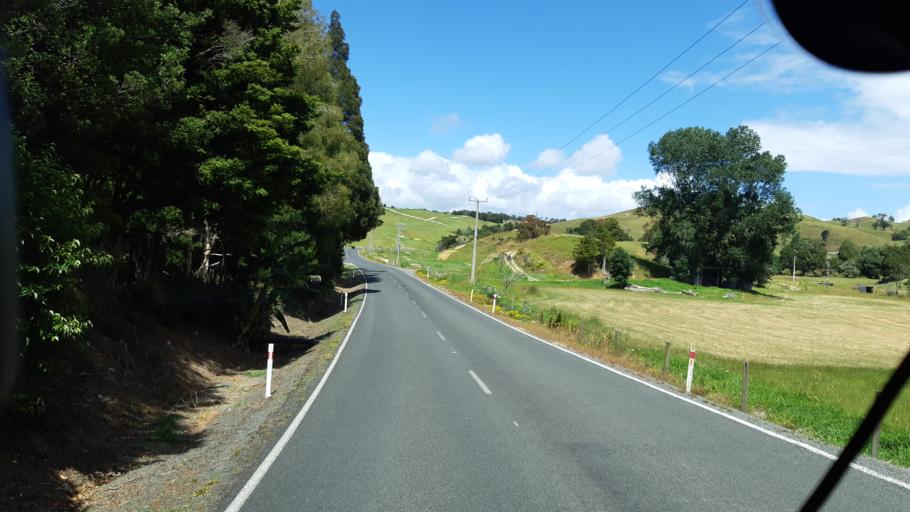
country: NZ
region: Northland
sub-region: Far North District
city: Taipa
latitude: -35.2691
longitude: 173.4922
